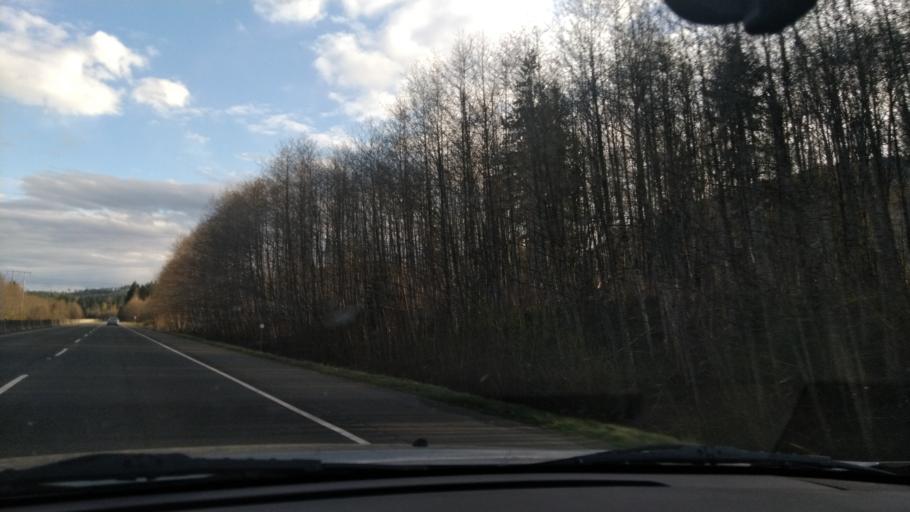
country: CA
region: British Columbia
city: Courtenay
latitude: 49.7422
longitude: -125.1192
